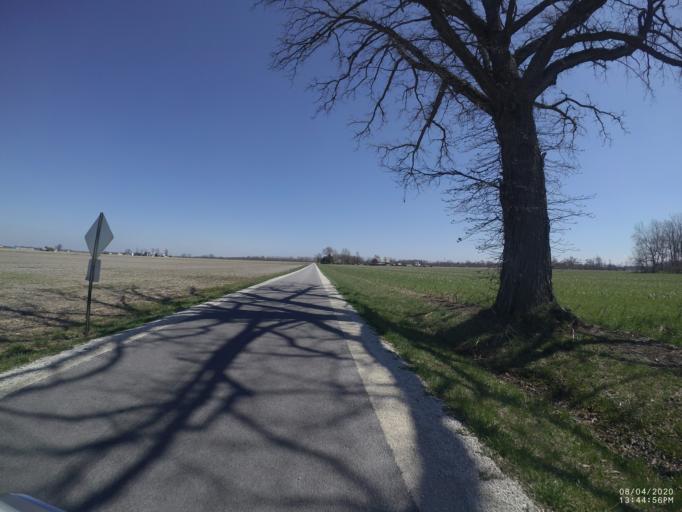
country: US
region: Ohio
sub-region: Sandusky County
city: Gibsonburg
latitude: 41.3266
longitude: -83.2994
